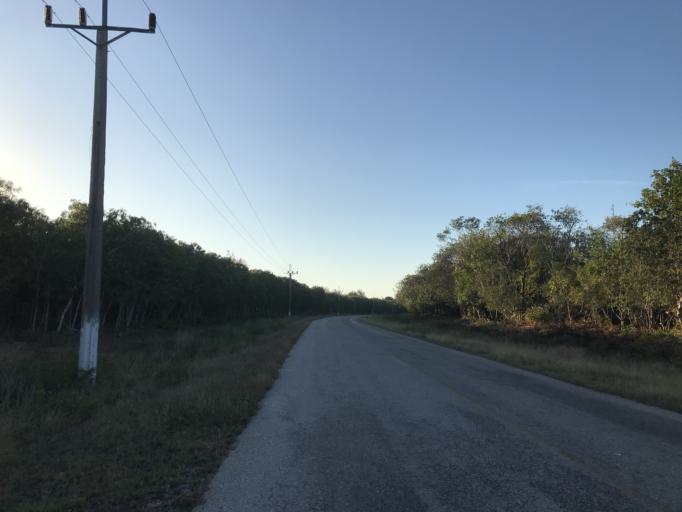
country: CU
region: Cienfuegos
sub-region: Municipio de Aguada de Pasajeros
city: Aguada de Pasajeros
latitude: 22.0675
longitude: -81.0471
